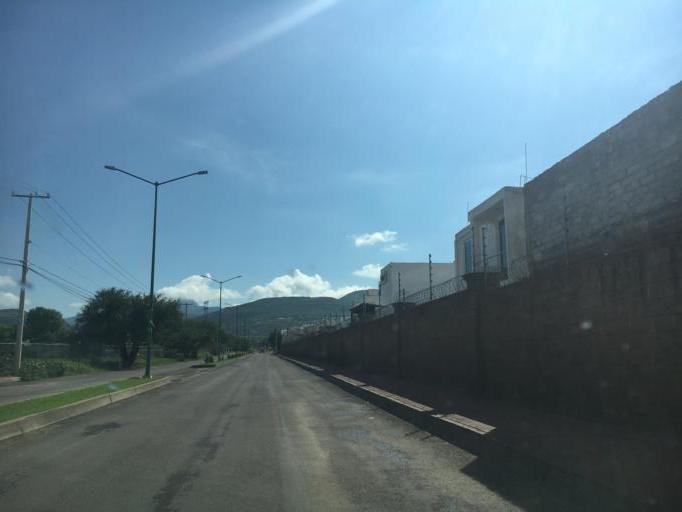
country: MX
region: Guanajuato
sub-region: Leon
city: Medina
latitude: 21.1304
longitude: -101.6177
